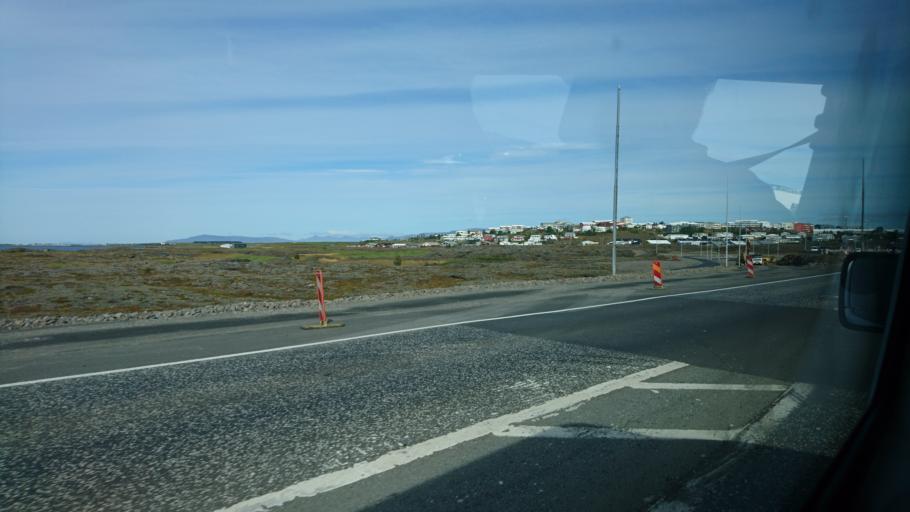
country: IS
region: Capital Region
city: Alftanes
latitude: 64.0513
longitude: -21.9986
